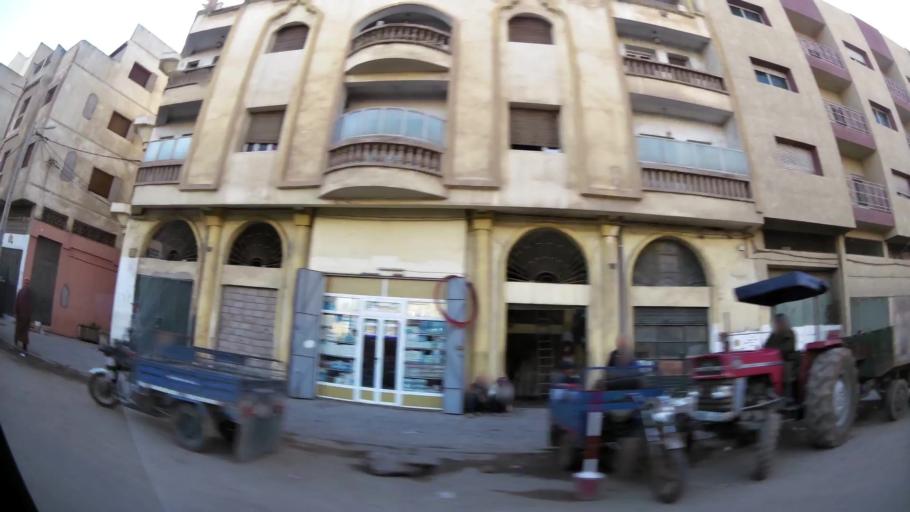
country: MA
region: Chaouia-Ouardigha
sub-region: Settat Province
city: Settat
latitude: 33.0019
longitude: -7.6158
